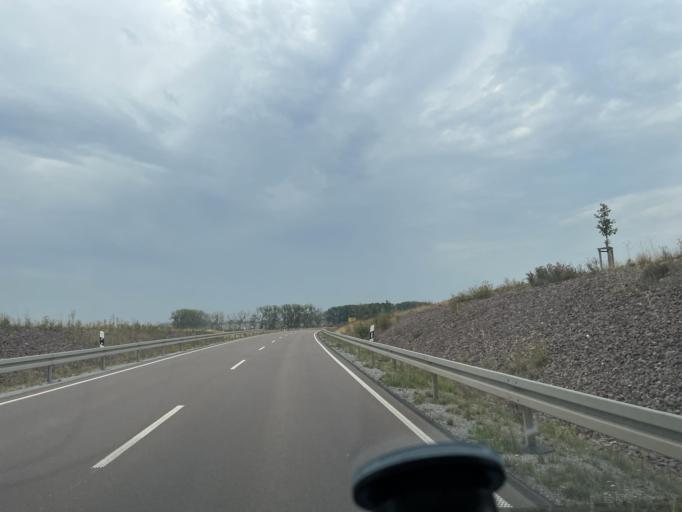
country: DE
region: Saxony-Anhalt
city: Brumby
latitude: 51.8892
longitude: 11.7225
